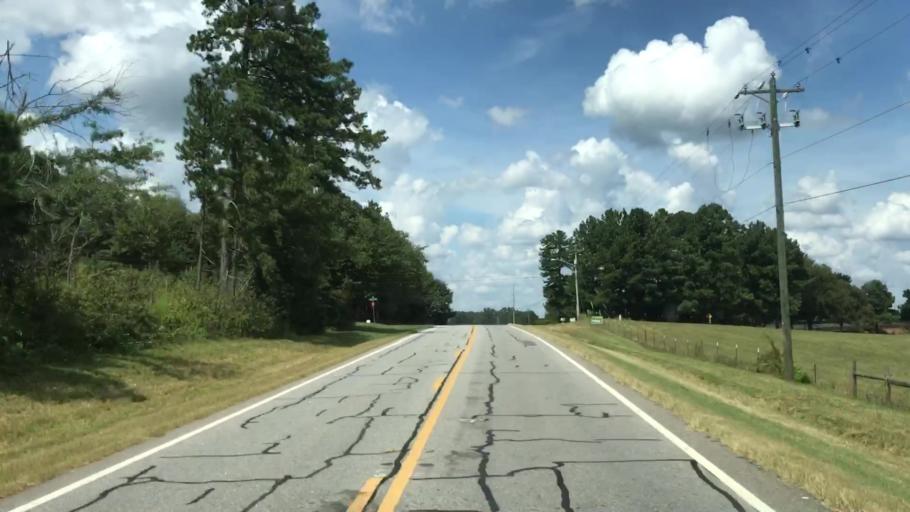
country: US
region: Georgia
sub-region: Oconee County
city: Watkinsville
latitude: 33.7904
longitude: -83.3215
